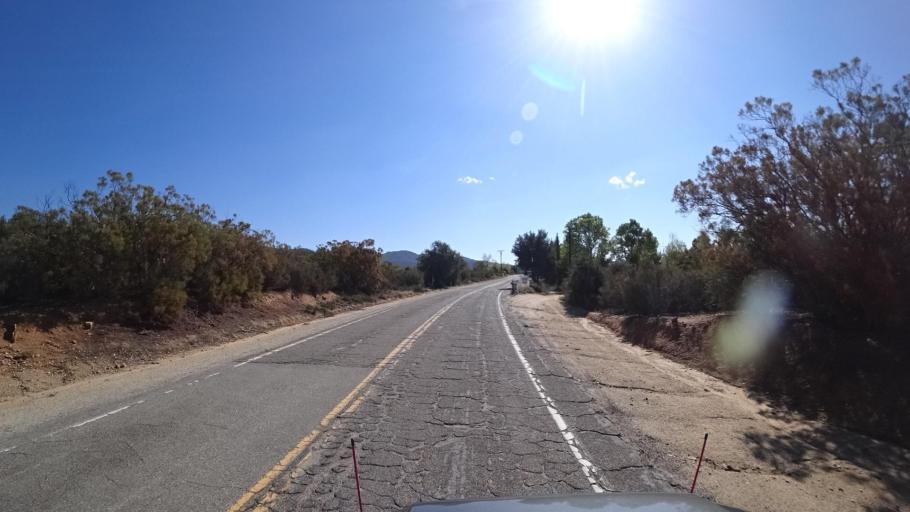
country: US
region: California
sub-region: Riverside County
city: Anza
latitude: 33.3862
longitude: -116.6657
